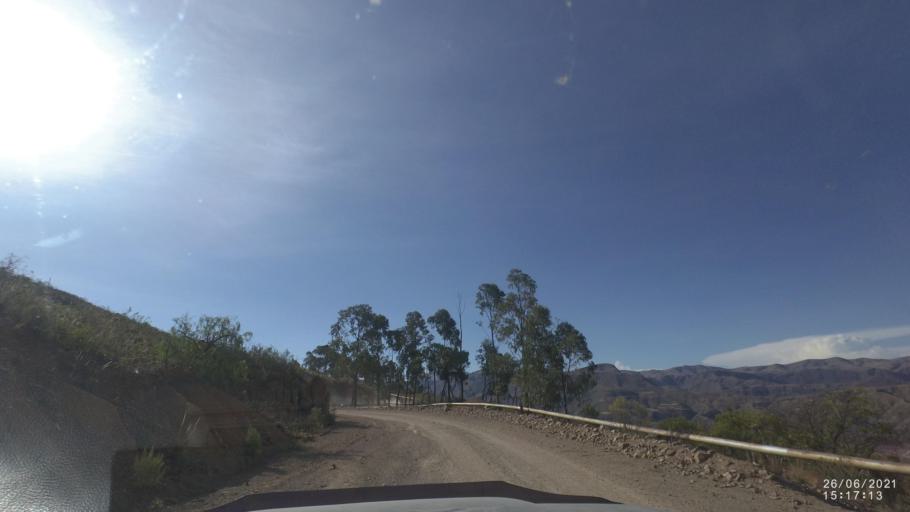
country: BO
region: Cochabamba
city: Mizque
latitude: -17.9532
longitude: -65.6513
